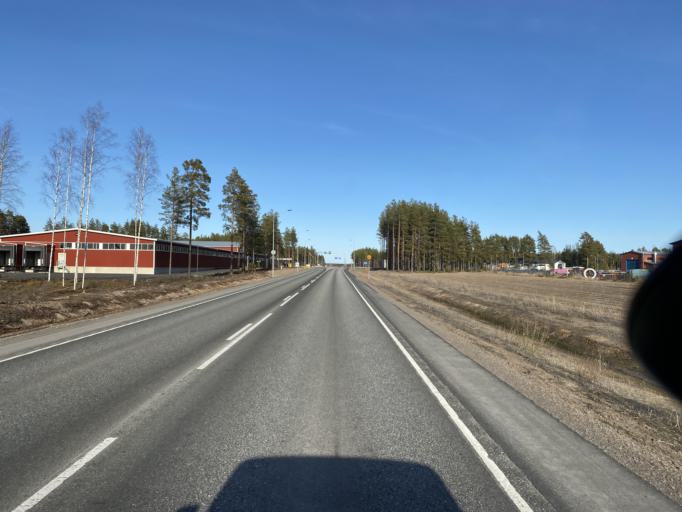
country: FI
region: Satakunta
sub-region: Rauma
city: Koeylioe
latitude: 61.1564
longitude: 22.2791
